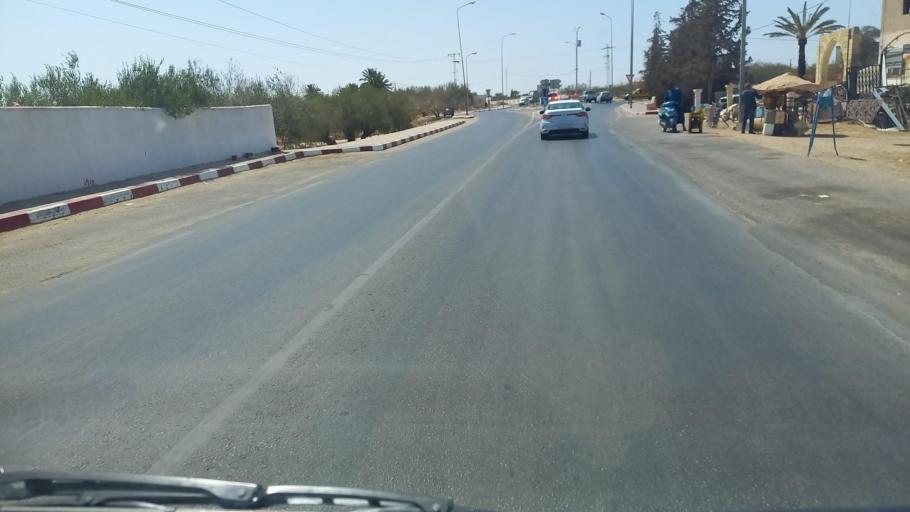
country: TN
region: Madanin
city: Houmt Souk
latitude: 33.8240
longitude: 10.8705
